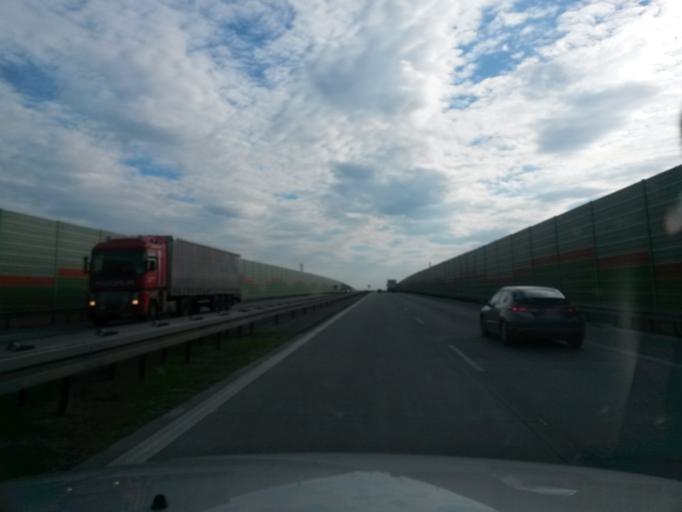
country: PL
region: Lodz Voivodeship
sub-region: Powiat tomaszowski
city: Tomaszow Mazowiecki
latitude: 51.5602
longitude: 20.0119
